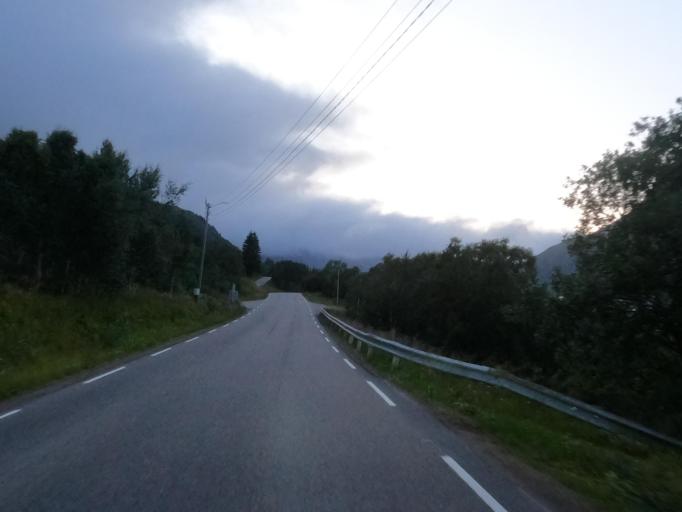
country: NO
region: Nordland
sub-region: Lodingen
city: Lodingen
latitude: 68.5839
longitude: 15.7919
